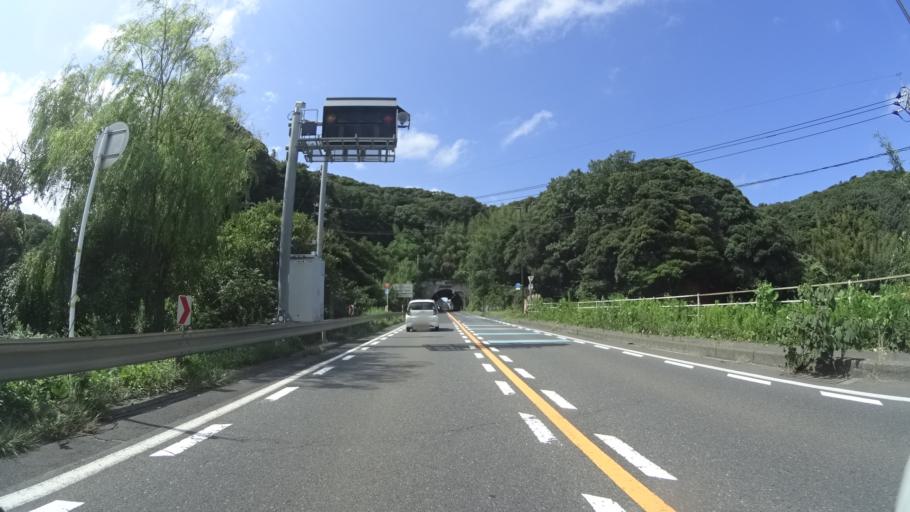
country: JP
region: Tottori
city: Tottori
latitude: 35.5209
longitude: 134.1022
